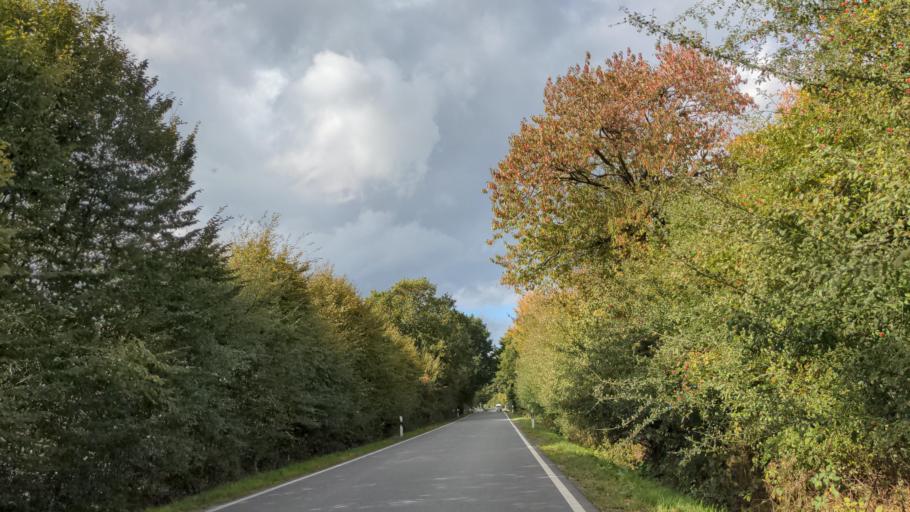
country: DE
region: Schleswig-Holstein
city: Stockelsdorf
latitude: 53.9298
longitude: 10.6054
